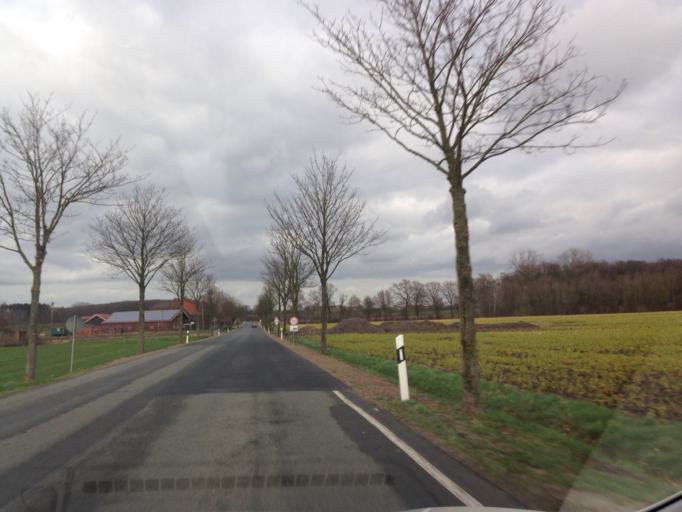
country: DE
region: North Rhine-Westphalia
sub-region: Regierungsbezirk Munster
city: Nordkirchen
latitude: 51.7678
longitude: 7.5391
